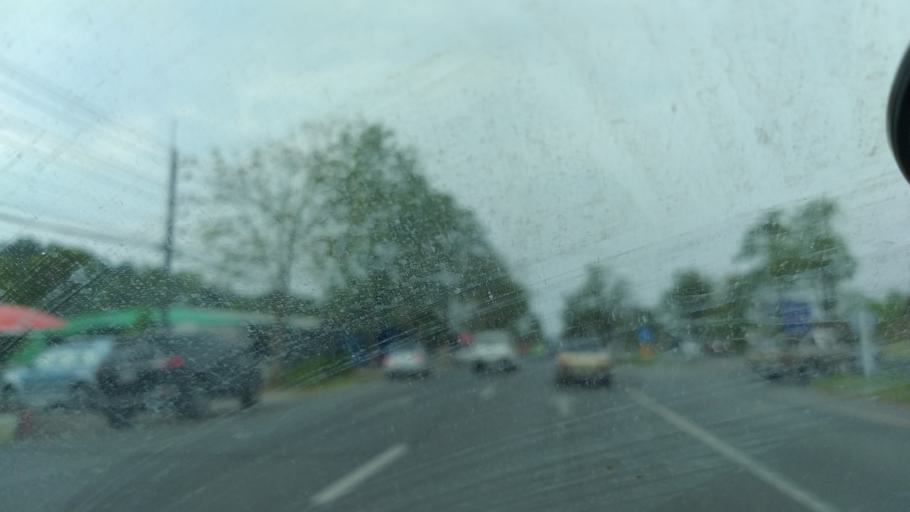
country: TH
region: Chanthaburi
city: Chanthaburi
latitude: 12.6576
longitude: 102.0596
